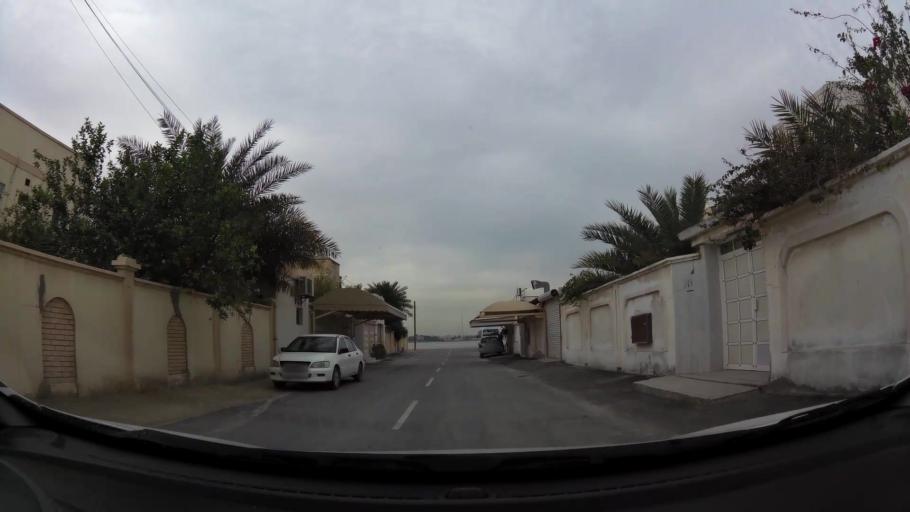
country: BH
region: Northern
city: Madinat `Isa
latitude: 26.1810
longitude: 50.5809
